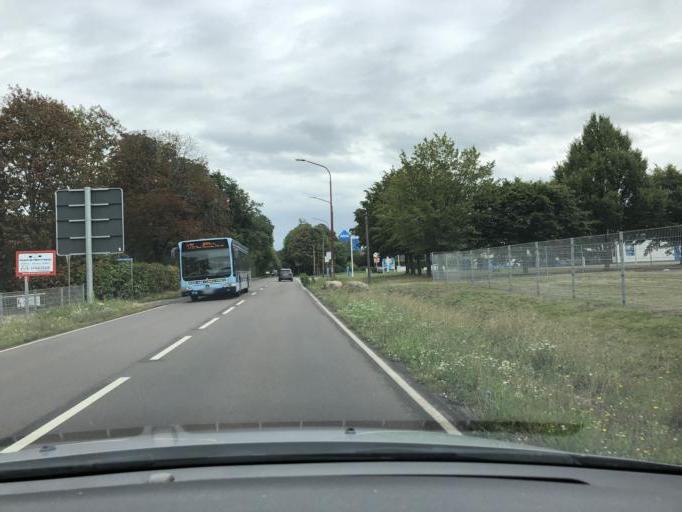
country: DE
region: Saxony-Anhalt
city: Koethen
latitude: 51.7554
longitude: 11.9472
